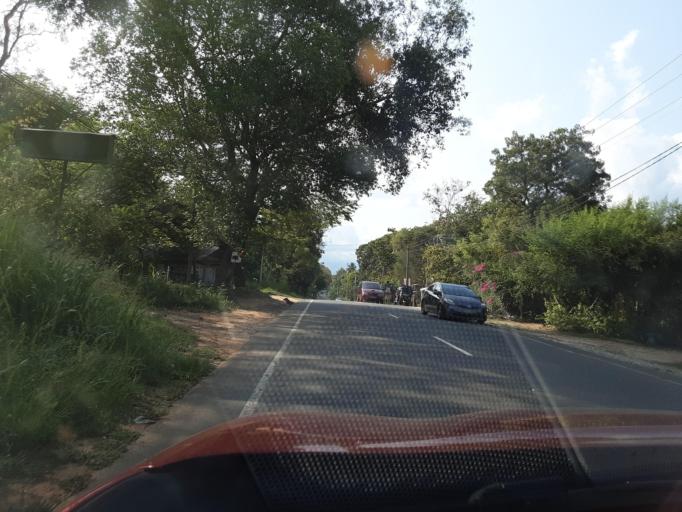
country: LK
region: Uva
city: Haputale
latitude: 6.6139
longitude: 81.1306
